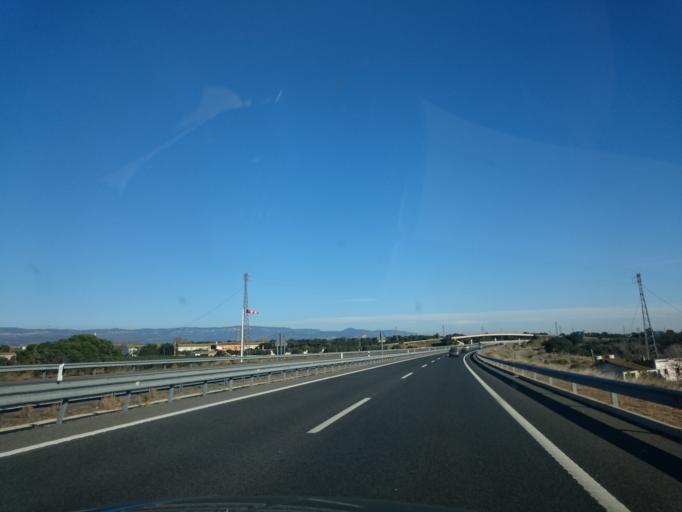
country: ES
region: Catalonia
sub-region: Provincia de Tarragona
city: Cambrils
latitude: 41.0731
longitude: 1.0148
